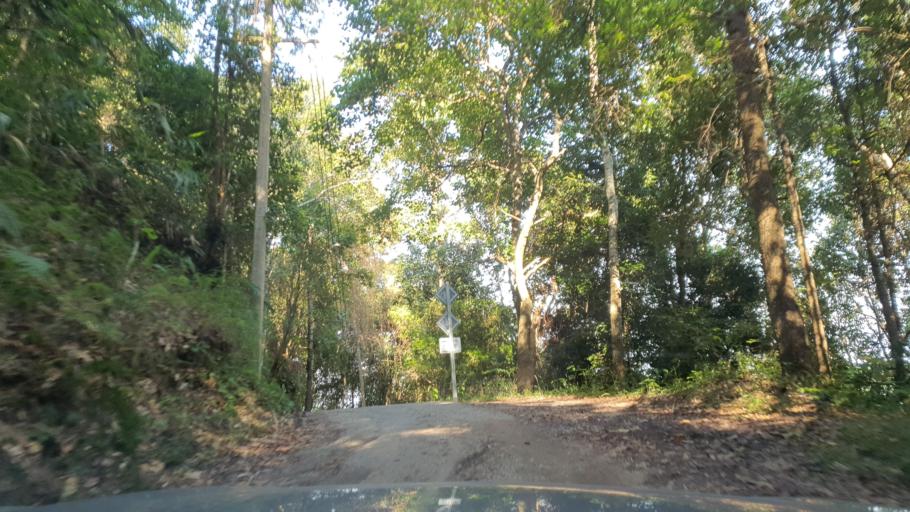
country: TH
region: Chiang Mai
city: Chiang Mai
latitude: 18.8335
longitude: 98.8973
